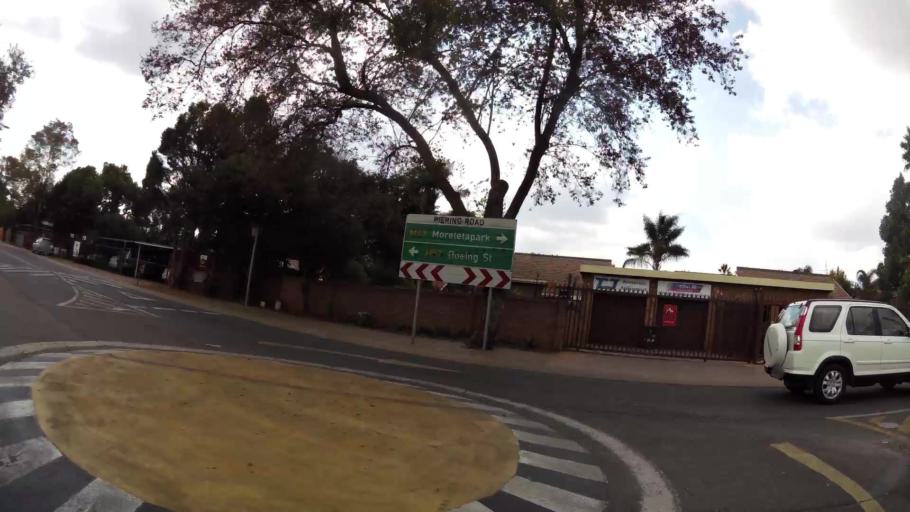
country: ZA
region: Gauteng
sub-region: City of Tshwane Metropolitan Municipality
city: Centurion
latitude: -25.8388
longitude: 28.2597
